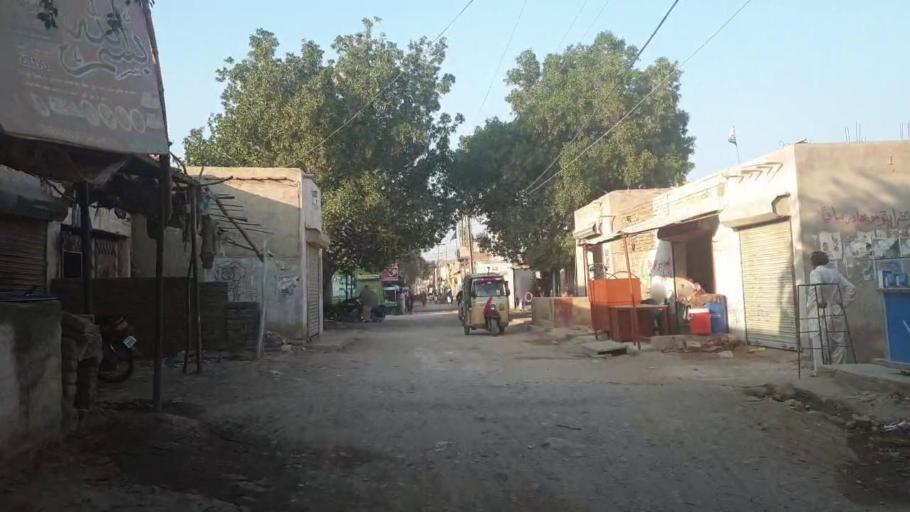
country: PK
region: Sindh
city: Jamshoro
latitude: 25.4428
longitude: 68.2959
